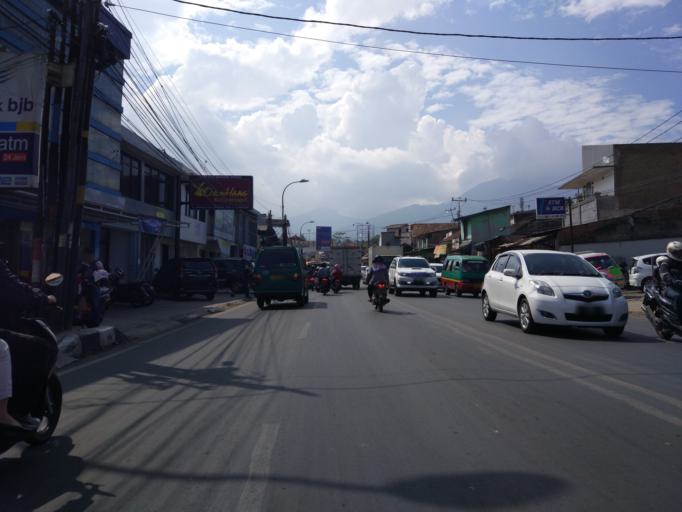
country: ID
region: West Java
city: Cileunyi
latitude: -6.9355
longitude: 107.7282
